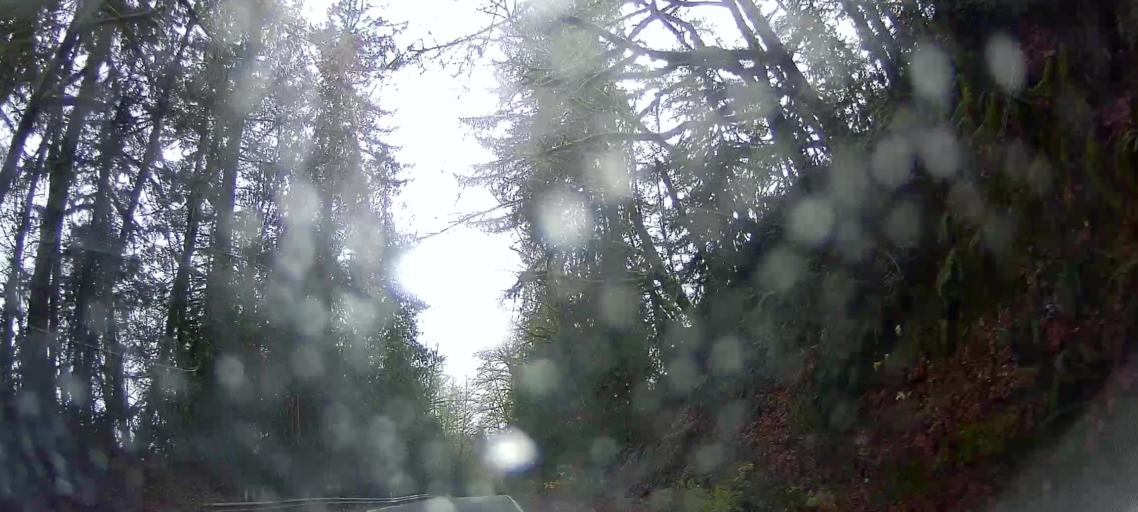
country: US
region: Washington
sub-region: Snohomish County
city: Darrington
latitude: 48.5264
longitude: -121.7759
